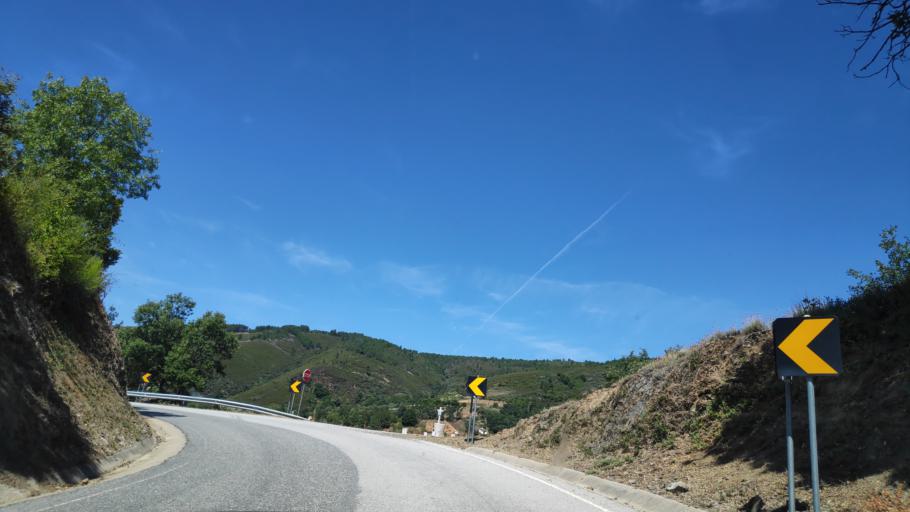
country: PT
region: Braganca
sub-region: Braganca Municipality
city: Braganca
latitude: 41.9011
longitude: -6.7287
